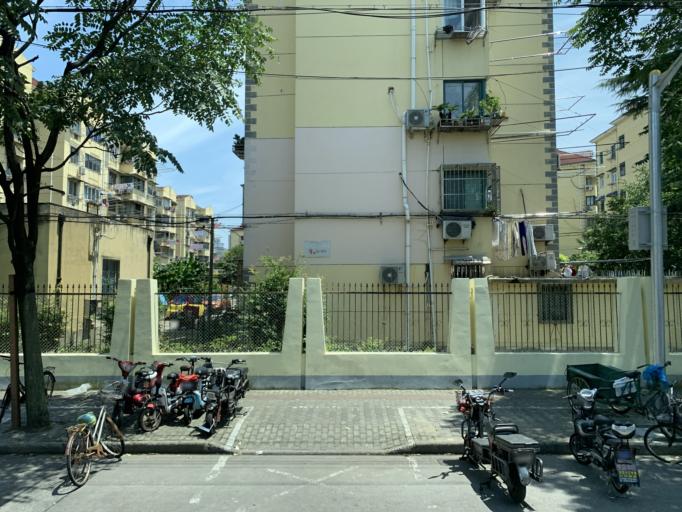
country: CN
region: Shanghai Shi
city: Huamu
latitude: 31.2480
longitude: 121.5765
